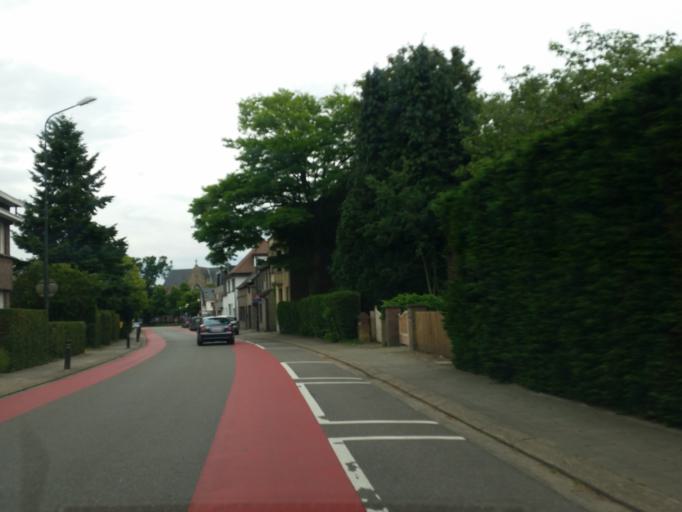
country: BE
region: Flanders
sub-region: Provincie Antwerpen
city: Schilde
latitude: 51.2337
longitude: 4.5823
